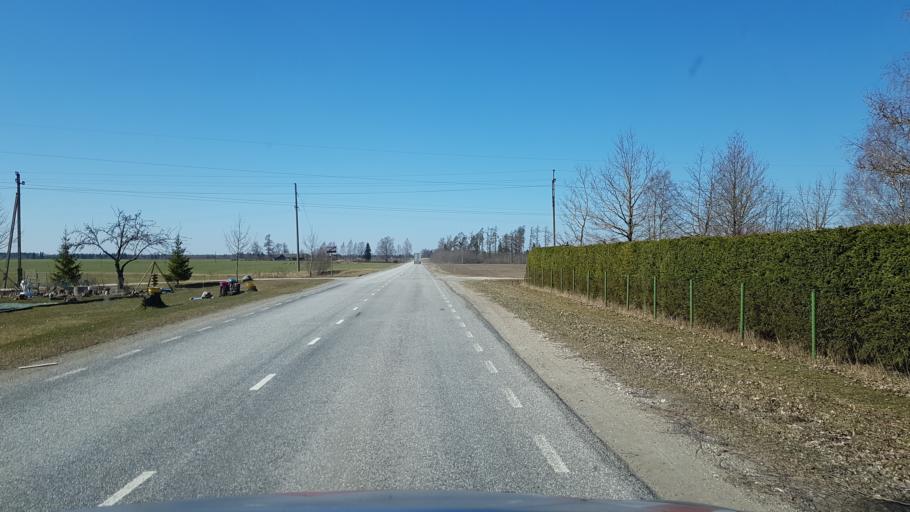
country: EE
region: Laeaene-Virumaa
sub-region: Vaeike-Maarja vald
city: Vaike-Maarja
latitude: 59.1355
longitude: 26.2505
